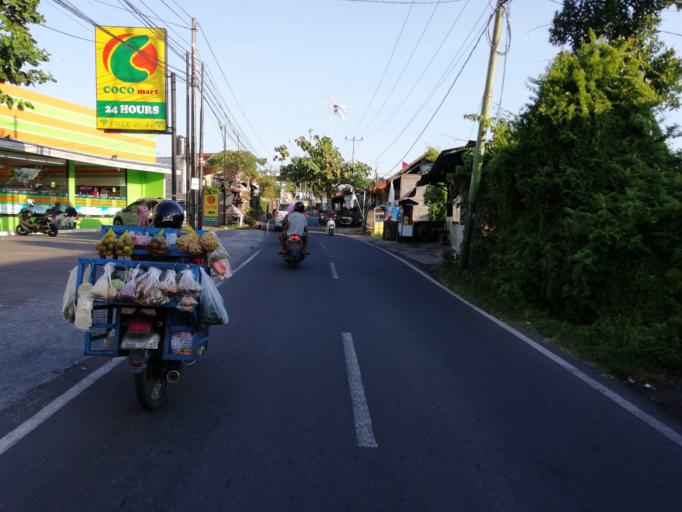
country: ID
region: Bali
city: Bualu
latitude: -8.7894
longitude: 115.1961
